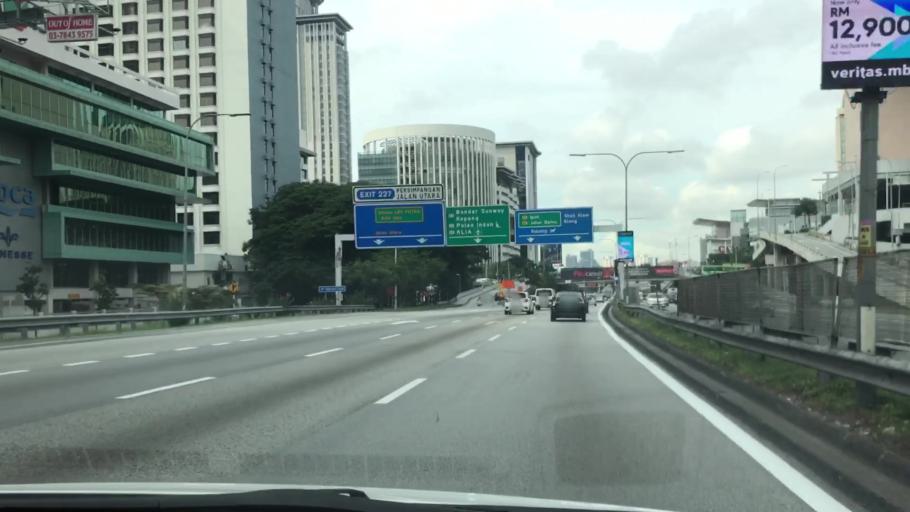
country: MY
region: Selangor
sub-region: Petaling
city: Petaling Jaya
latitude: 3.1039
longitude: 101.6419
